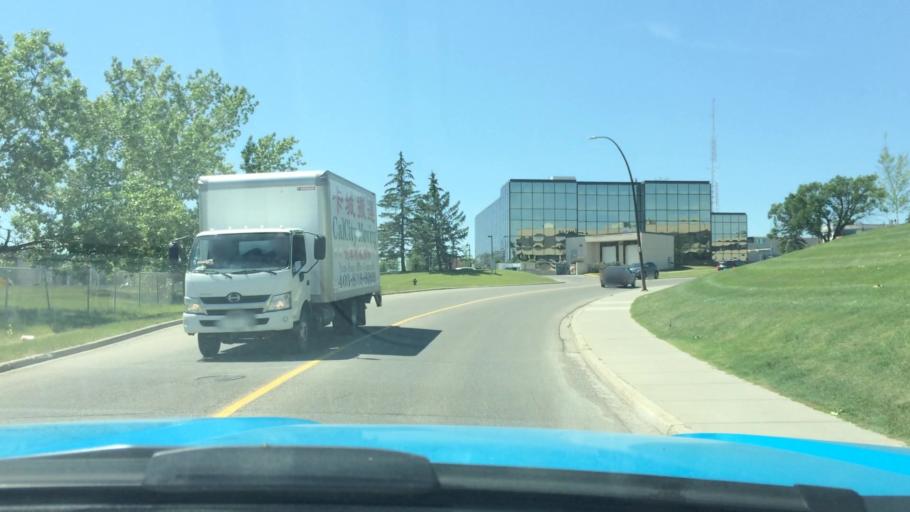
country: CA
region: Alberta
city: Calgary
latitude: 51.0506
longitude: -113.9892
